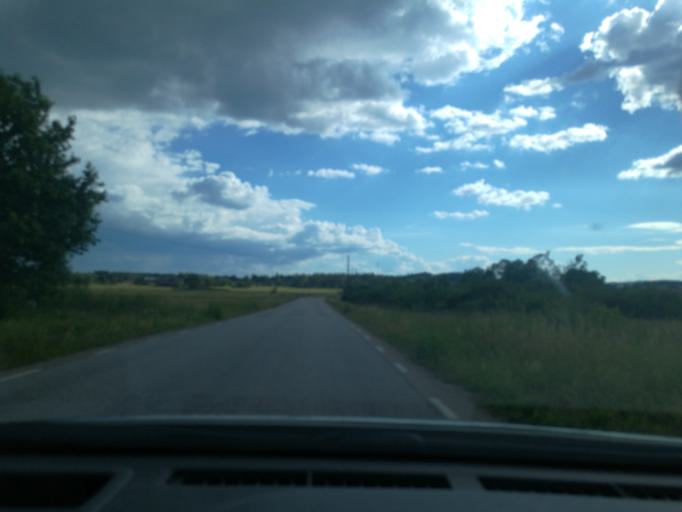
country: SE
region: Soedermanland
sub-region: Eskilstuna Kommun
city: Arla
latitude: 59.4069
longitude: 16.6881
